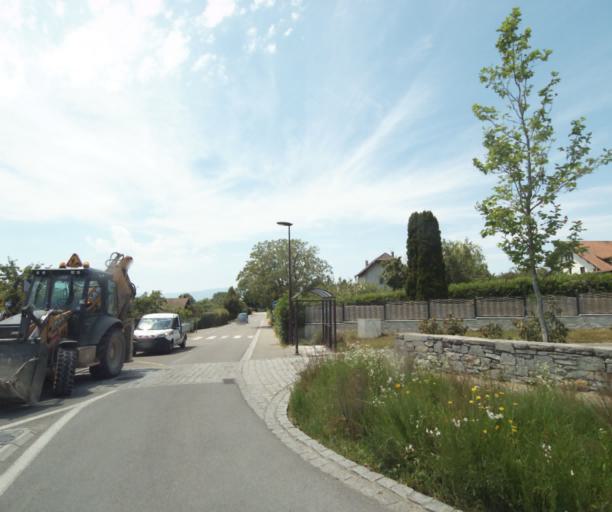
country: FR
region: Rhone-Alpes
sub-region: Departement de la Haute-Savoie
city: Messery
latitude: 46.3537
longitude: 6.3172
